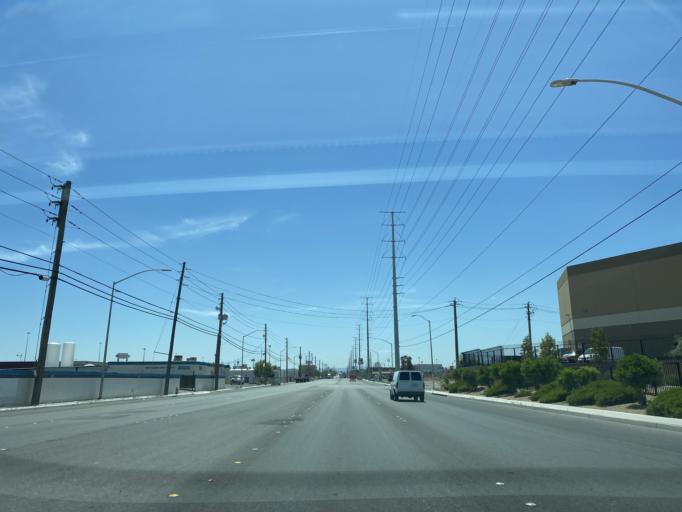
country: US
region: Nevada
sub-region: Clark County
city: North Las Vegas
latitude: 36.2258
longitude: -115.1214
